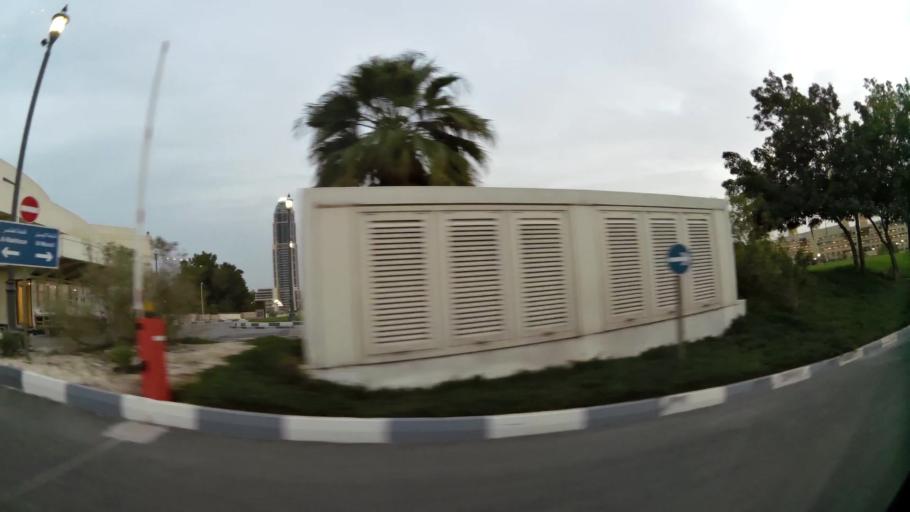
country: QA
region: Baladiyat ad Dawhah
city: Doha
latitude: 25.3793
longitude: 51.5305
